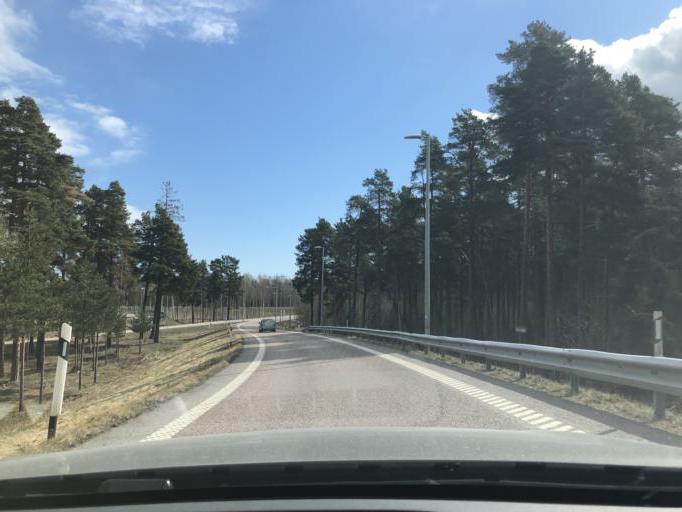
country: SE
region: Gaevleborg
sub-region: Gavle Kommun
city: Gavle
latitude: 60.6689
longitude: 17.0913
